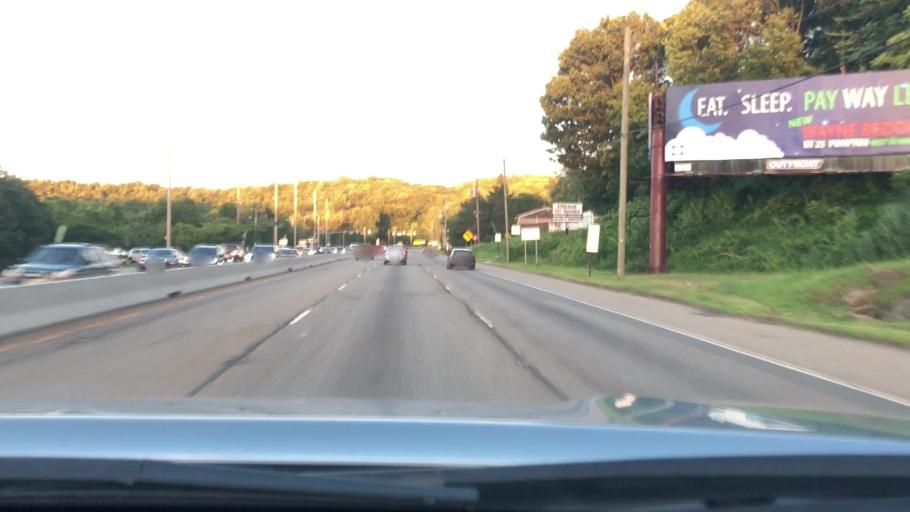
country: US
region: New Jersey
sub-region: Passaic County
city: Bloomingdale
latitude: 40.9886
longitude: -74.3303
